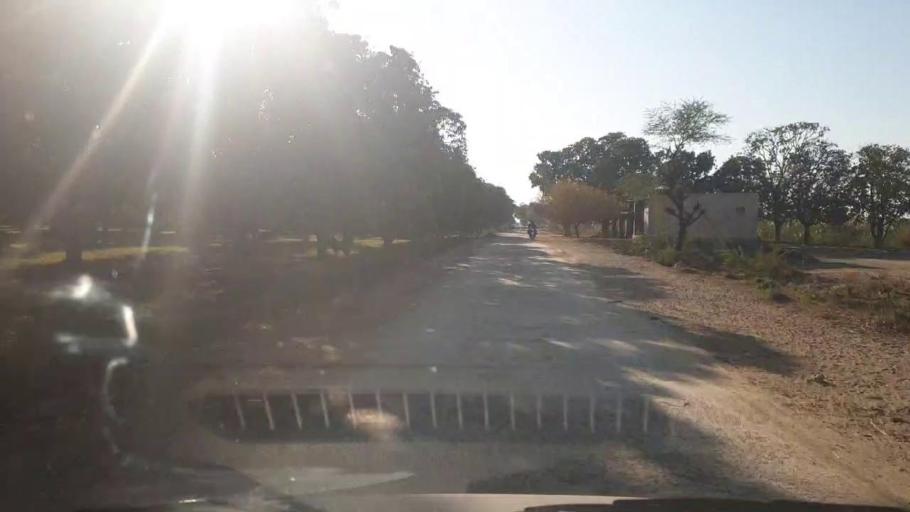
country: PK
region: Sindh
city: Samaro
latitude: 25.3406
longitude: 69.3071
